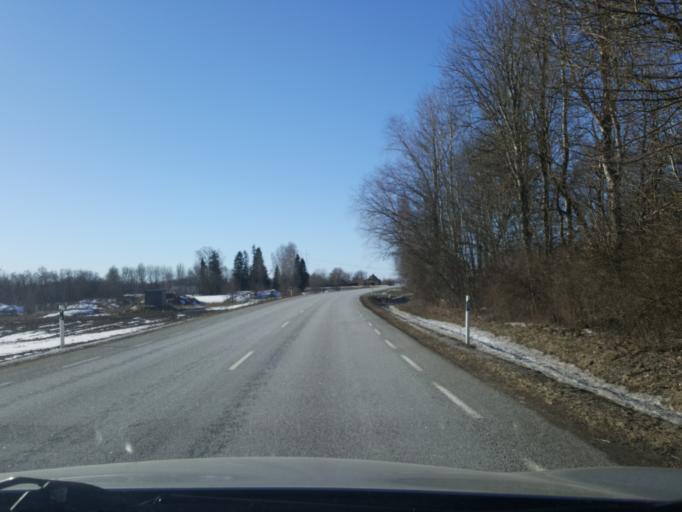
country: EE
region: Viljandimaa
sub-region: Viiratsi vald
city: Viiratsi
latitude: 58.3975
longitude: 25.6440
